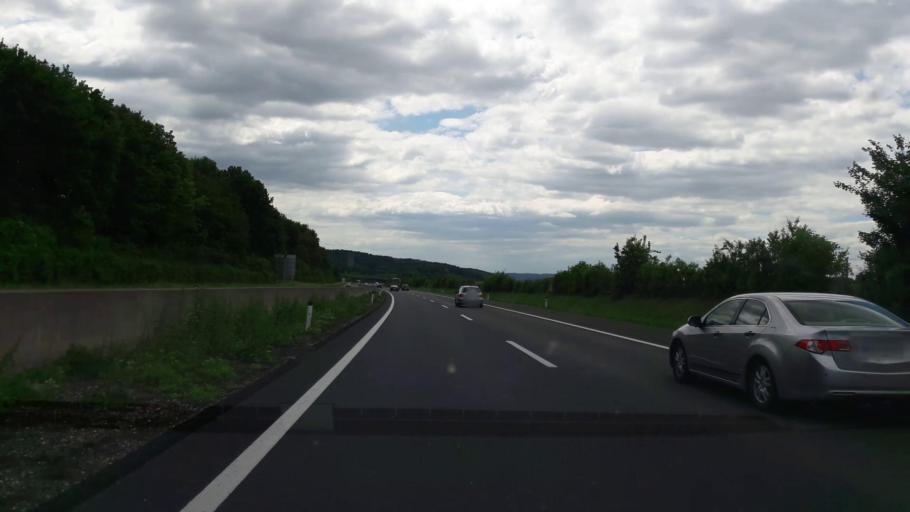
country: AT
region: Styria
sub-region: Politischer Bezirk Hartberg-Fuerstenfeld
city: Sankt Johann in der Haide
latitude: 47.2634
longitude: 16.0007
